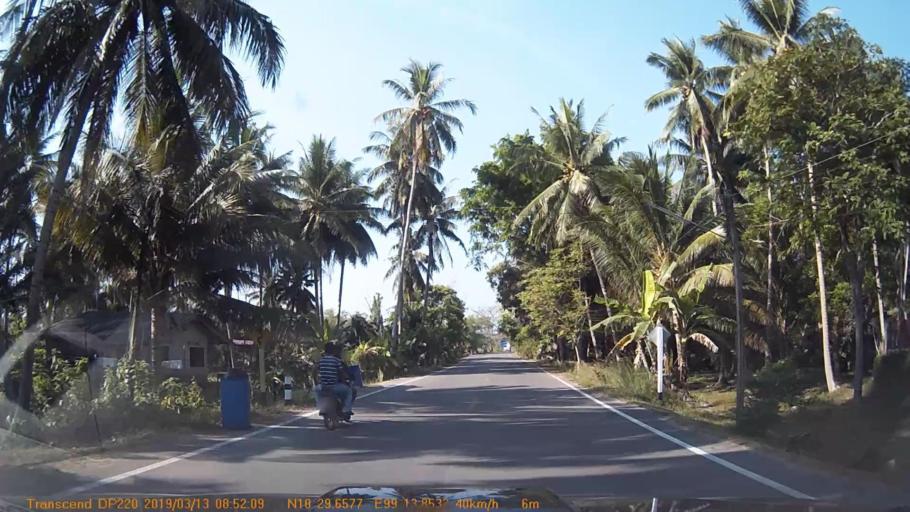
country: TH
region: Chumphon
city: Chumphon
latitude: 10.4940
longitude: 99.2308
